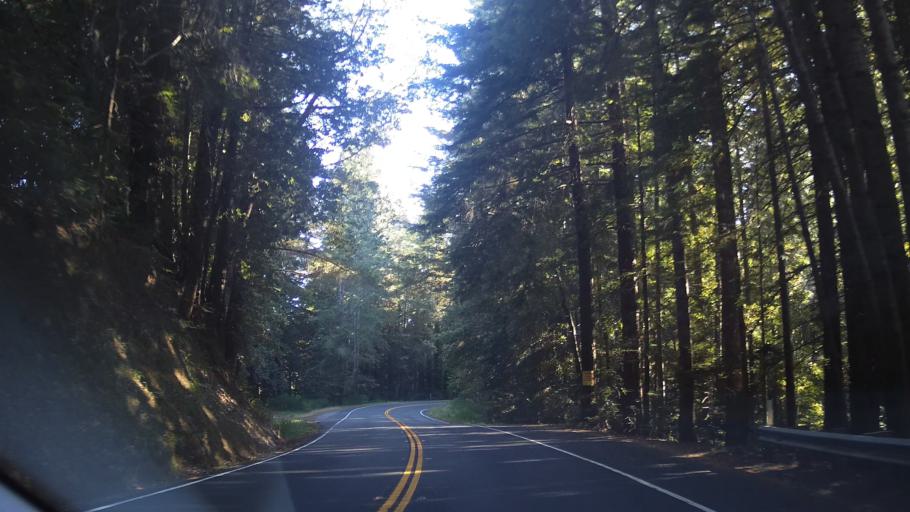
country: US
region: California
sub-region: Mendocino County
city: Fort Bragg
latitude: 39.3585
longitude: -123.6247
